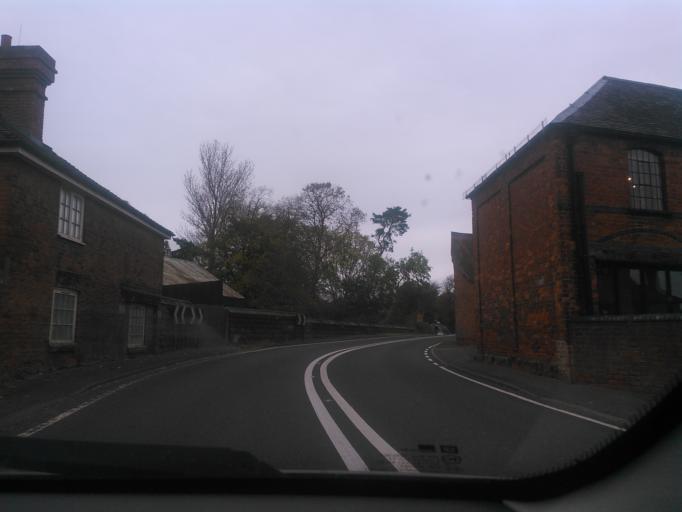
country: GB
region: England
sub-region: Shropshire
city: Astley
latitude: 52.7592
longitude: -2.7474
